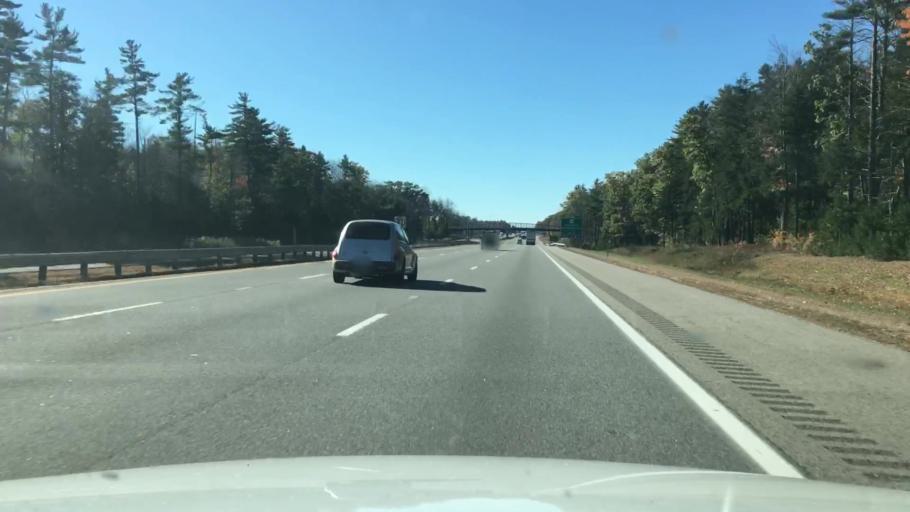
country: US
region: Maine
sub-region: York County
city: West Kennebunk
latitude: 43.4213
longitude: -70.5537
